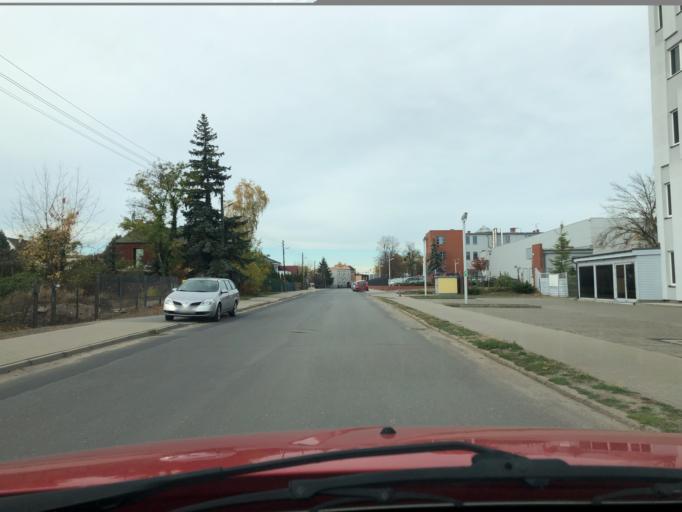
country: PL
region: Greater Poland Voivodeship
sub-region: Powiat poznanski
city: Plewiska
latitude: 52.3796
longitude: 16.8378
